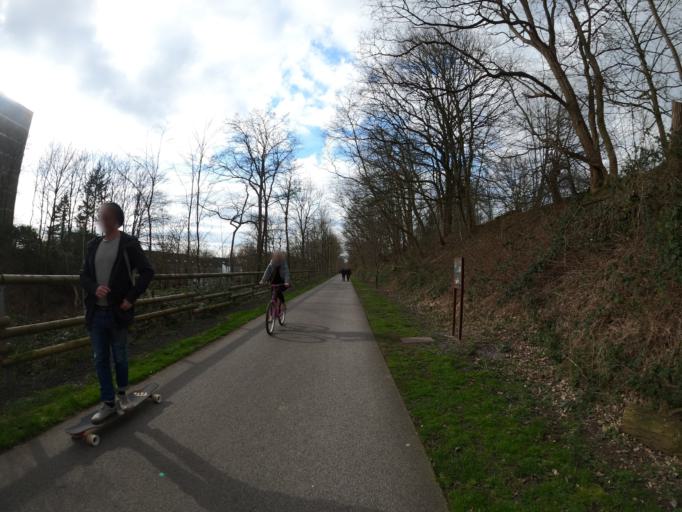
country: DE
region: North Rhine-Westphalia
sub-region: Regierungsbezirk Dusseldorf
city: Solingen
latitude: 51.1849
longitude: 7.0607
